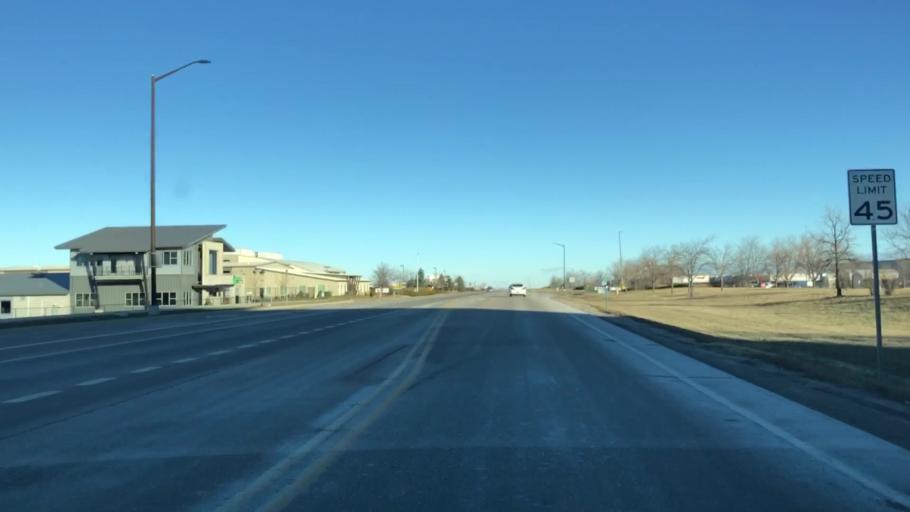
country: US
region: Colorado
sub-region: Weld County
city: Windsor
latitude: 40.4359
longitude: -104.9726
